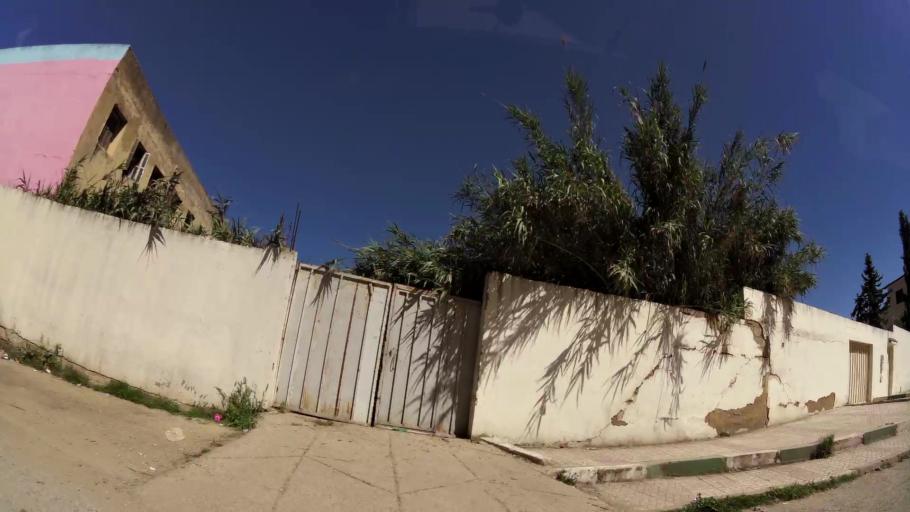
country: MA
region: Meknes-Tafilalet
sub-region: Meknes
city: Meknes
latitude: 33.8890
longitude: -5.5753
